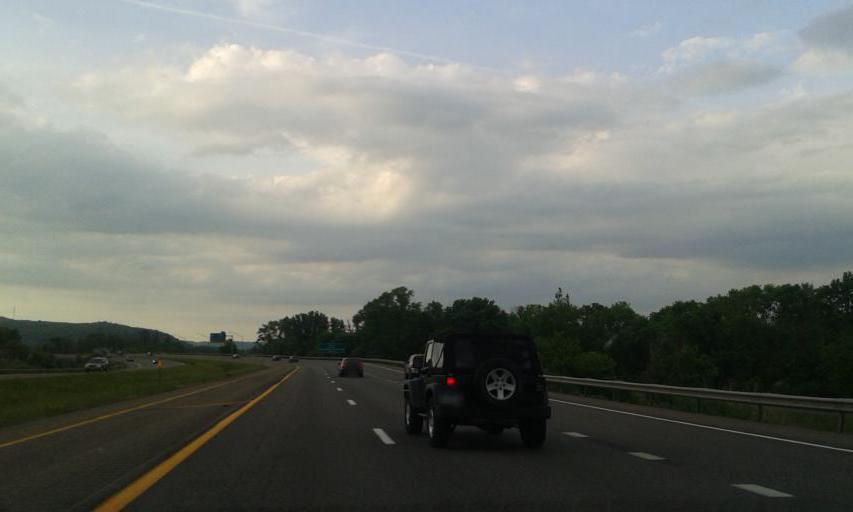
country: US
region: New York
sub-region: Broome County
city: Port Dickinson
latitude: 42.1472
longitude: -75.8979
